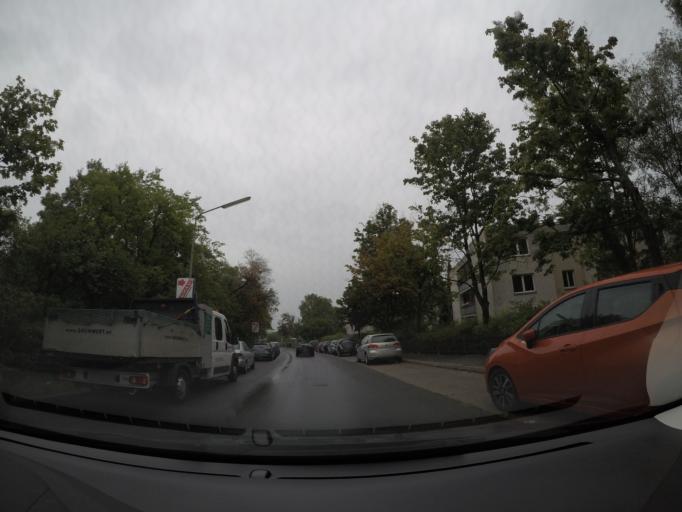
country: AT
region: Lower Austria
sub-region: Politischer Bezirk Modling
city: Perchtoldsdorf
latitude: 48.1585
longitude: 16.2892
